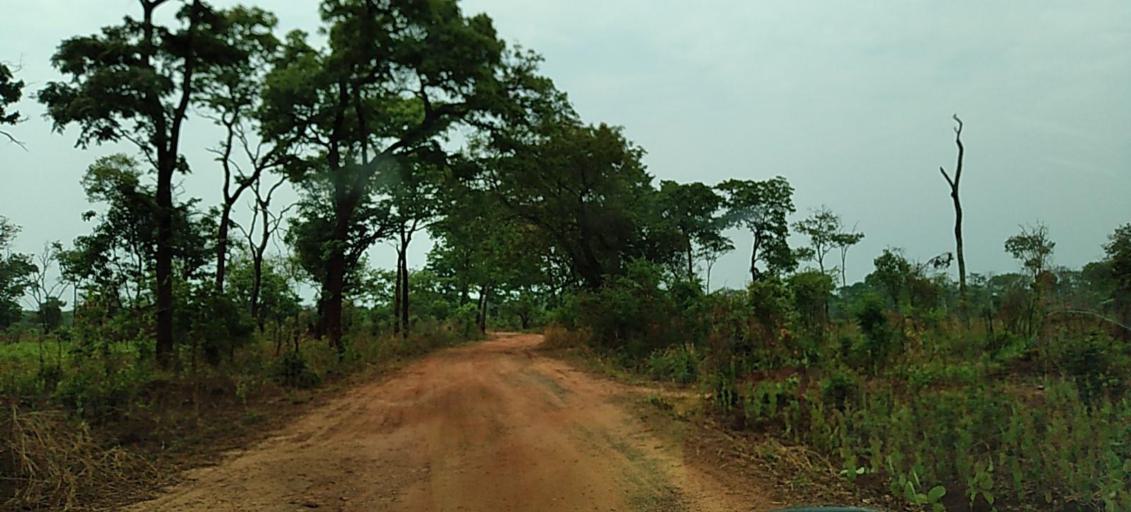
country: ZM
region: North-Western
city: Solwezi
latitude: -12.3355
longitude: 26.5231
